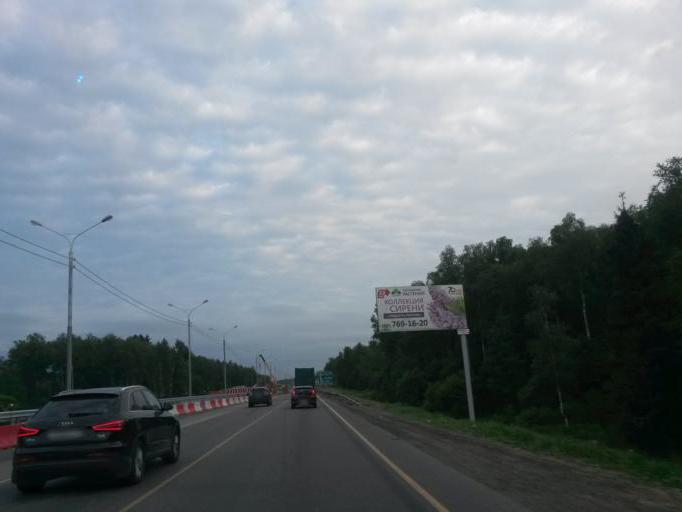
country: RU
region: Moskovskaya
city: Lyubuchany
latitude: 55.1983
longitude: 37.5346
